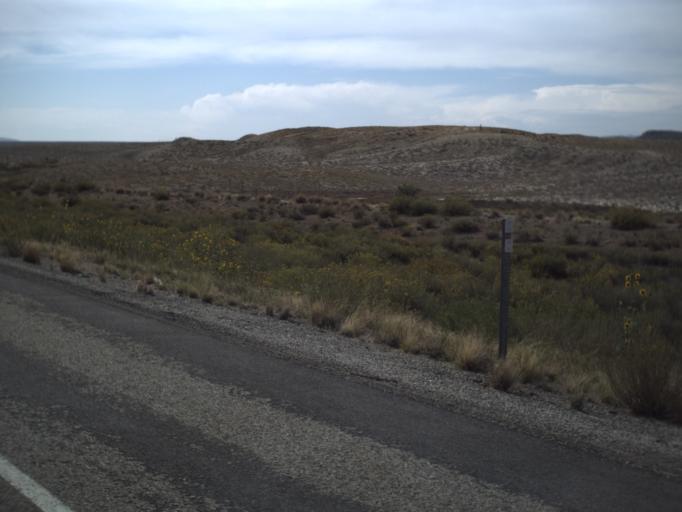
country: US
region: Utah
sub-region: Grand County
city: Moab
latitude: 38.9369
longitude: -109.4117
